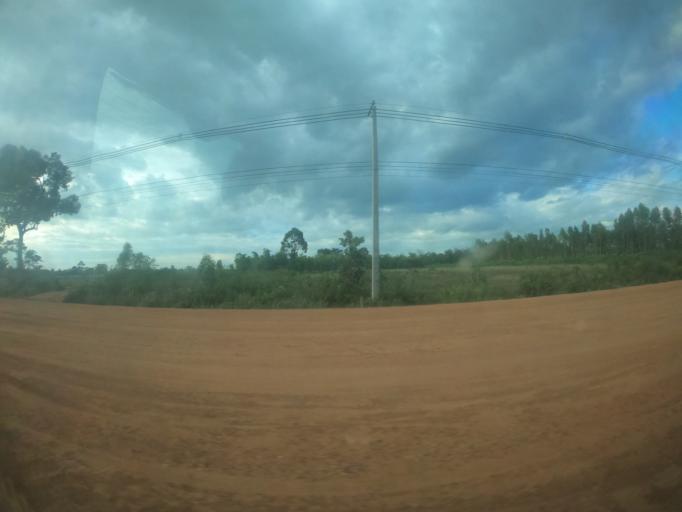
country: TH
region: Surin
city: Kap Choeng
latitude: 14.4578
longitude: 103.6713
